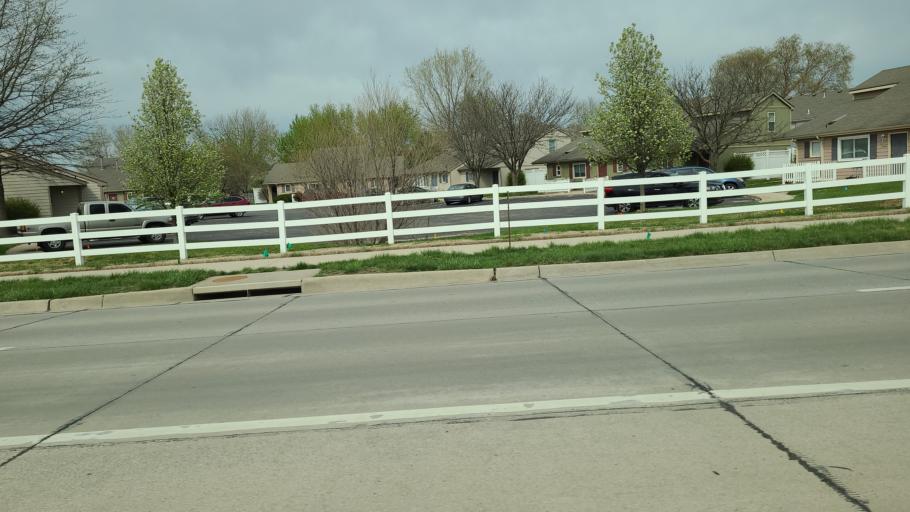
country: US
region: Kansas
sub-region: Douglas County
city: Lawrence
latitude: 38.9284
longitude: -95.2783
